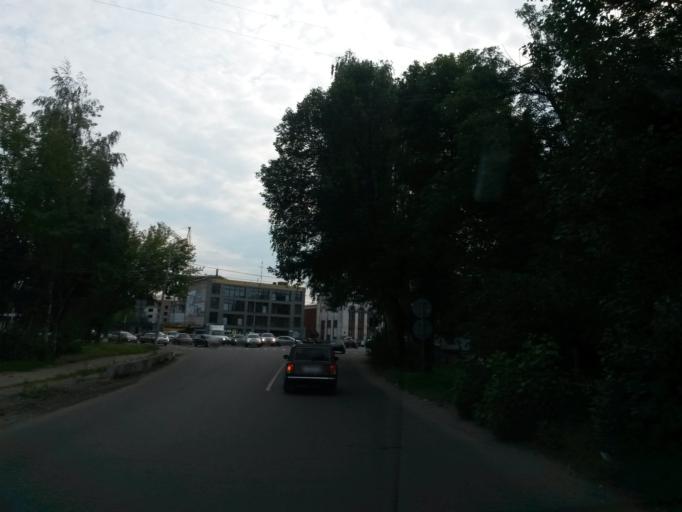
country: RU
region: Jaroslavl
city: Yaroslavl
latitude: 57.6092
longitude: 39.8365
